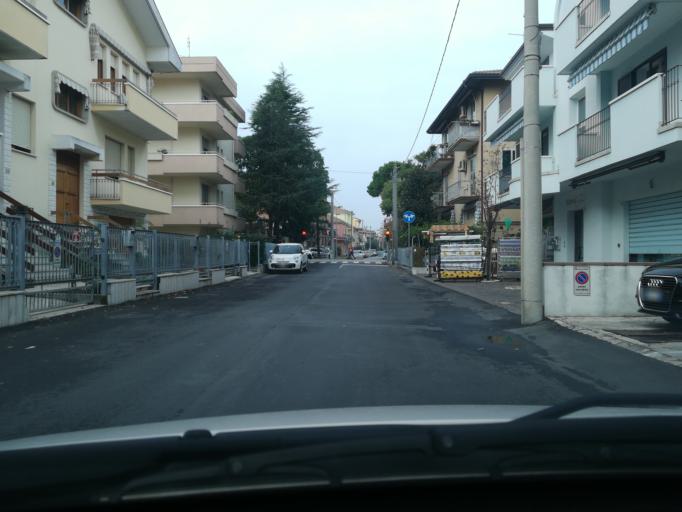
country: IT
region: Emilia-Romagna
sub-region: Provincia di Rimini
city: Rivazzurra
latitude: 44.0467
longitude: 12.5939
